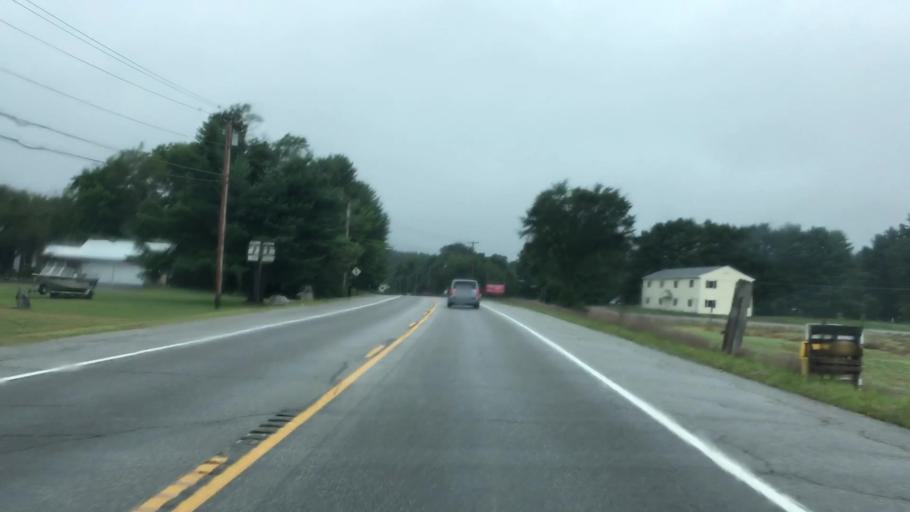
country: US
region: Maine
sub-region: Cumberland County
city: Raymond
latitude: 43.9569
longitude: -70.5607
